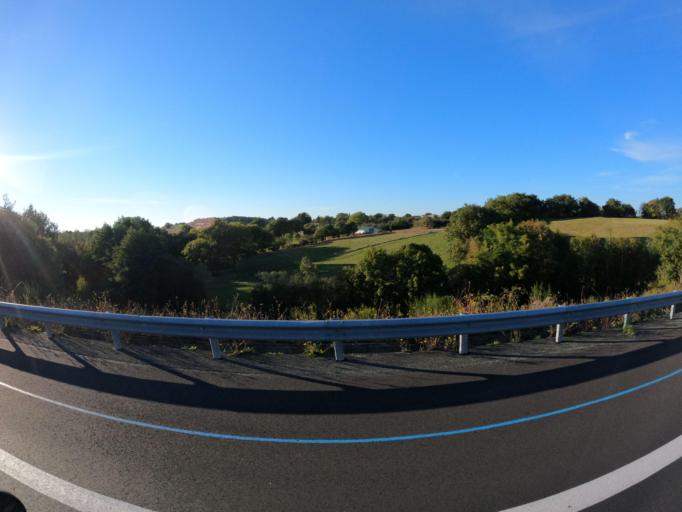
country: FR
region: Pays de la Loire
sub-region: Departement de la Vendee
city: Chambretaud
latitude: 46.9485
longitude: -0.9471
